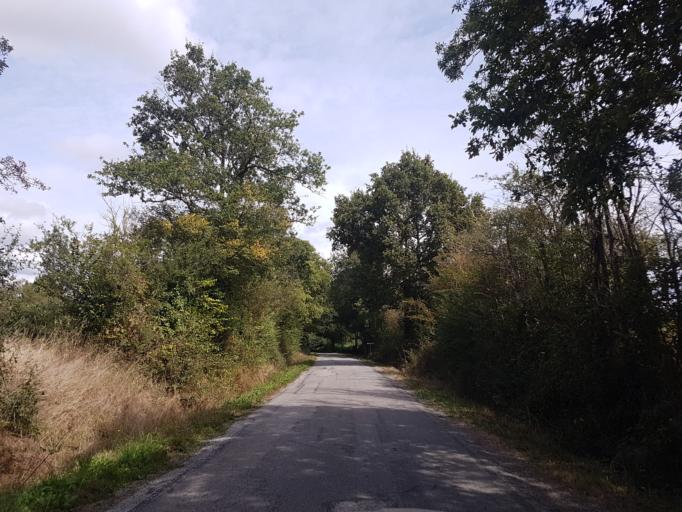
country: FR
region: Pays de la Loire
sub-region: Departement de la Loire-Atlantique
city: Petit-Mars
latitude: 47.3942
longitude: -1.4287
